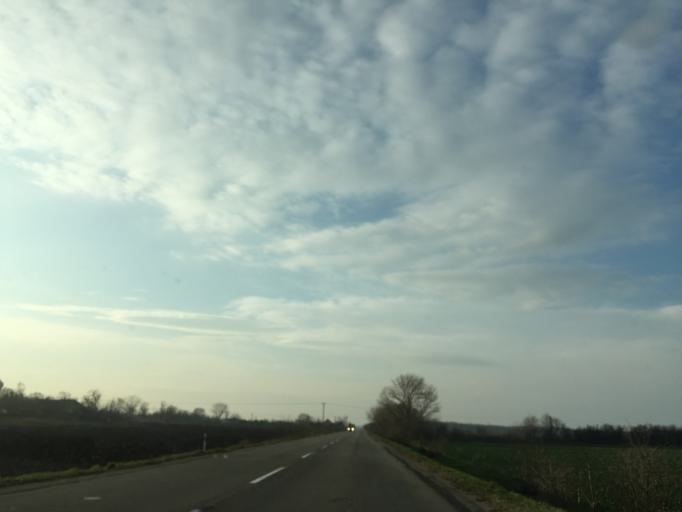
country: SK
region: Nitriansky
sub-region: Okres Komarno
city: Hurbanovo
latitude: 47.9176
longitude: 18.2666
